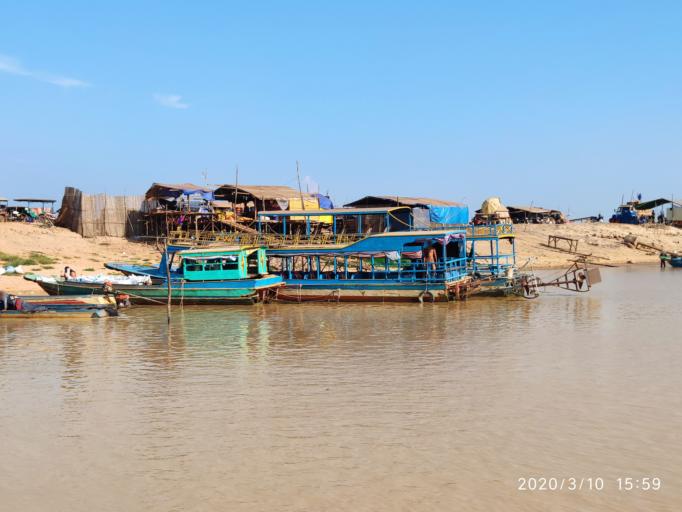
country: KH
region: Siem Reap
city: Siem Reap
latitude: 13.2636
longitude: 103.8223
